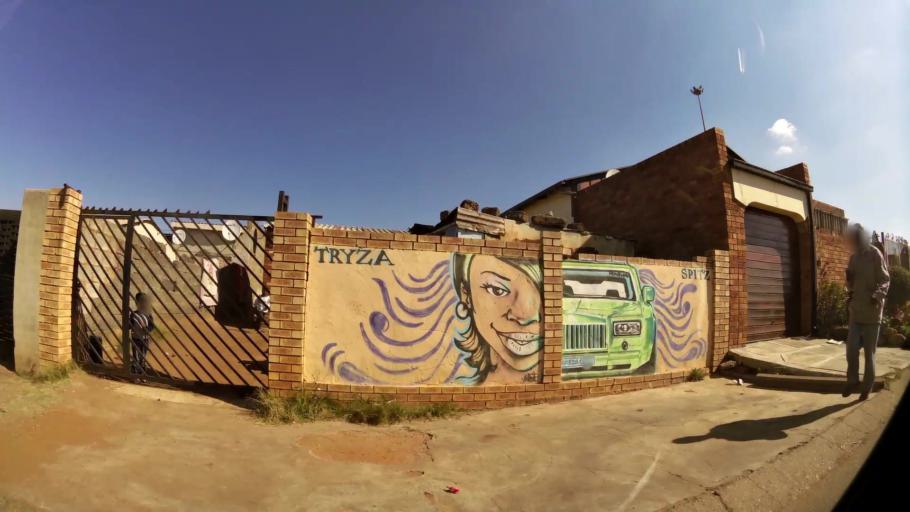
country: ZA
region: Gauteng
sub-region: City of Johannesburg Metropolitan Municipality
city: Soweto
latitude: -26.2353
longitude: 27.8839
